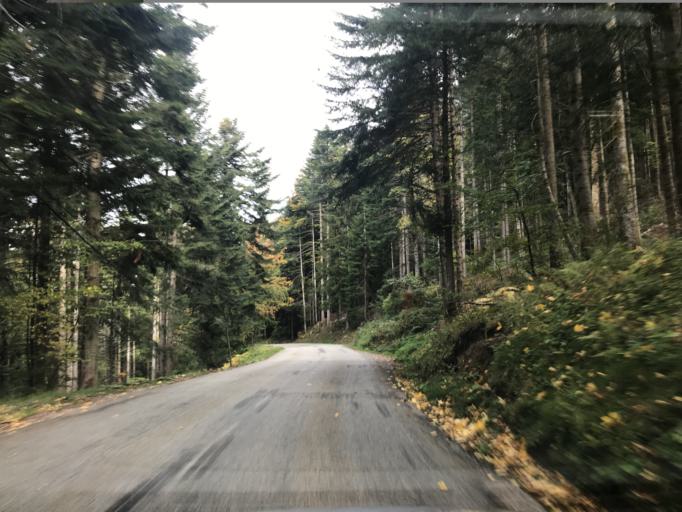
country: FR
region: Rhone-Alpes
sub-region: Departement de la Savoie
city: Les Echelles
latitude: 45.4552
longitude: 5.8208
